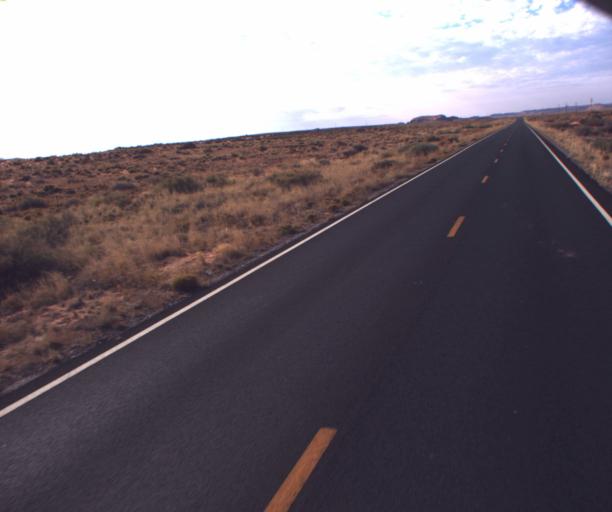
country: US
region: Arizona
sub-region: Apache County
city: Many Farms
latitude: 36.8043
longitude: -109.6482
